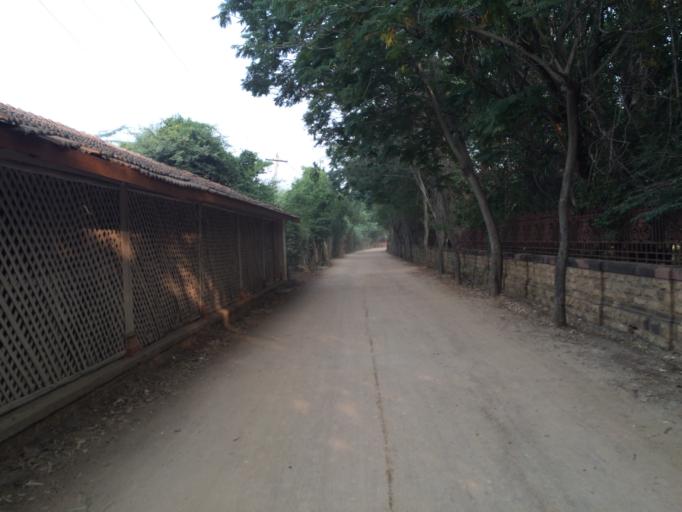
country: IN
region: Gujarat
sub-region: Kachchh
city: Mandvi
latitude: 22.8357
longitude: 69.2857
